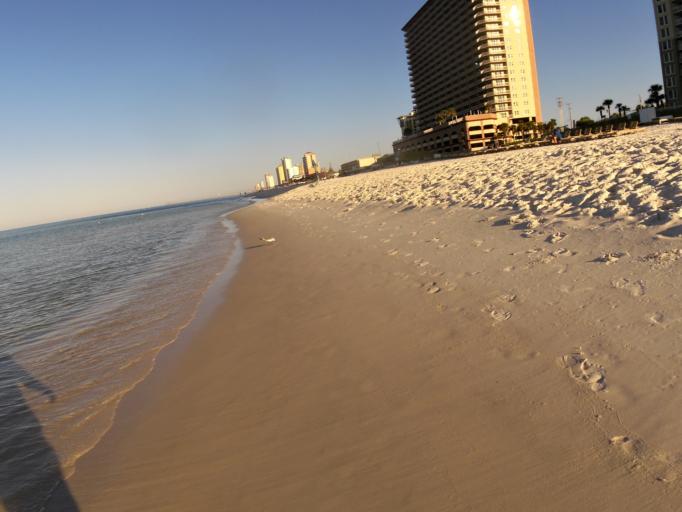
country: US
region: Florida
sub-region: Bay County
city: Panama City Beach
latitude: 30.2053
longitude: -85.8596
